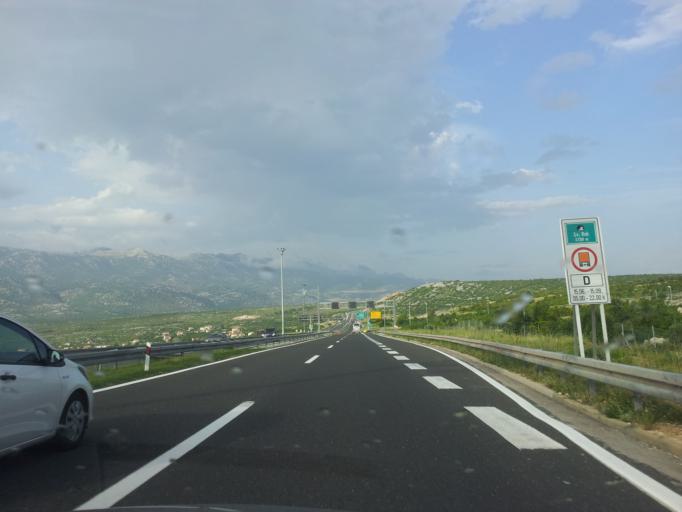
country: HR
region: Zadarska
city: Posedarje
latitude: 44.2375
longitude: 15.5268
